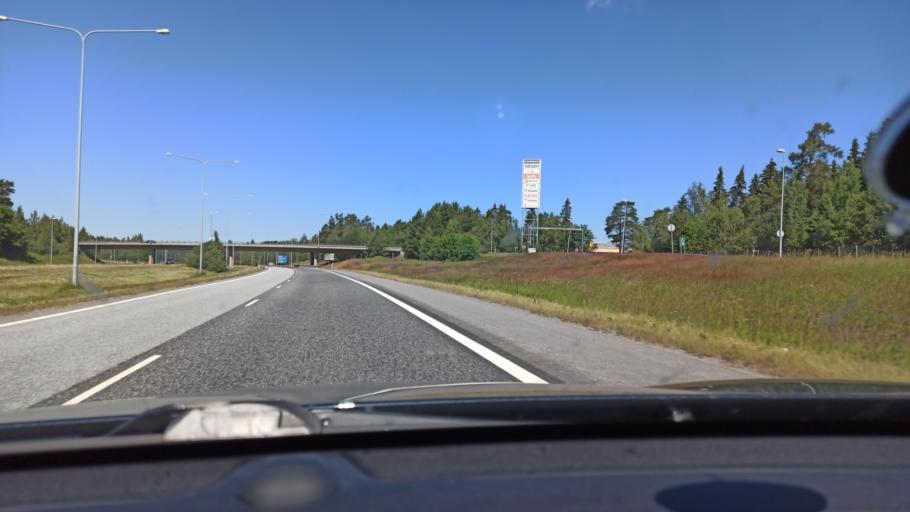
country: FI
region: Ostrobothnia
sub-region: Vaasa
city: Teeriniemi
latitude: 63.0693
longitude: 21.6995
